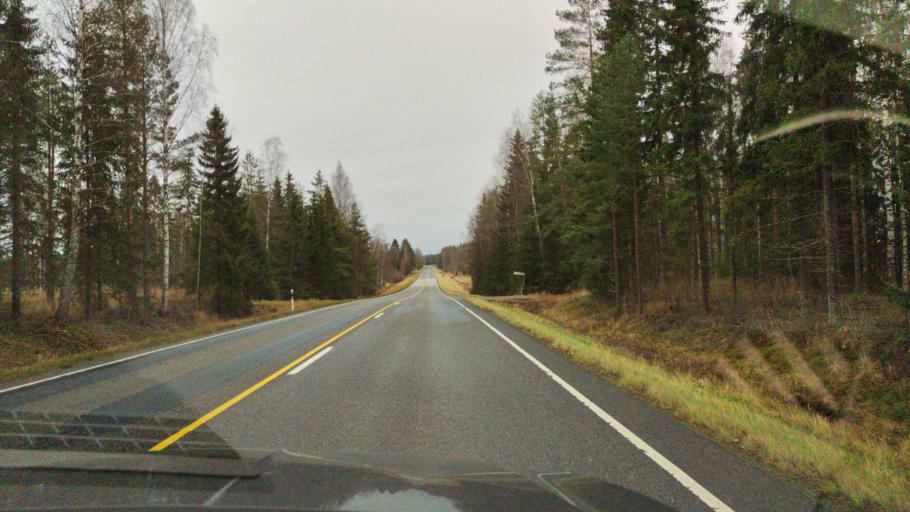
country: FI
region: Varsinais-Suomi
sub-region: Loimaa
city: Ylaene
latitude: 60.7726
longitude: 22.4393
